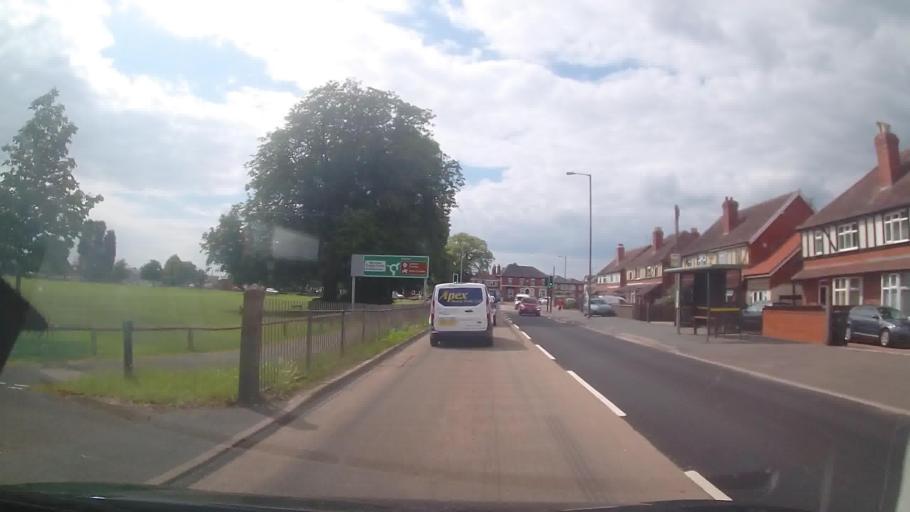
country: GB
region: England
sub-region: Herefordshire
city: Hereford
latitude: 52.0649
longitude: -2.7209
